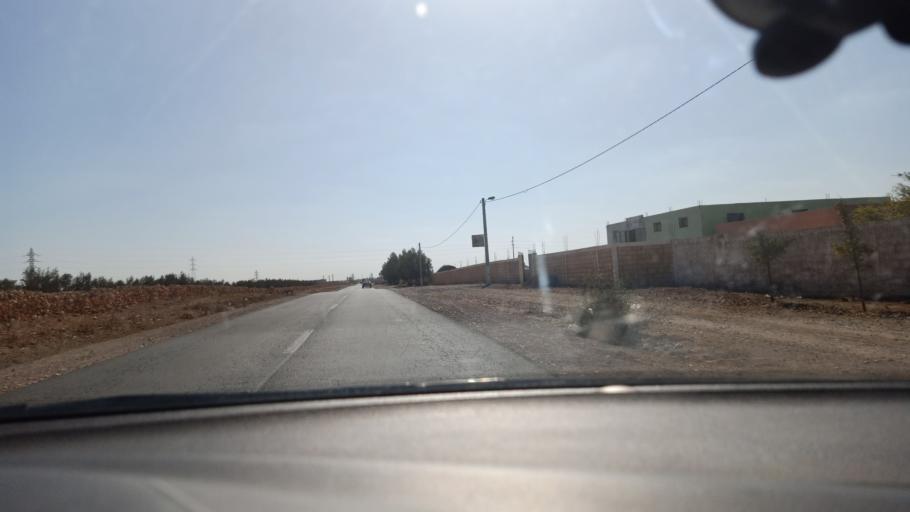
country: MA
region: Doukkala-Abda
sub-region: Safi
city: Youssoufia
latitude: 32.1170
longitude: -8.6056
